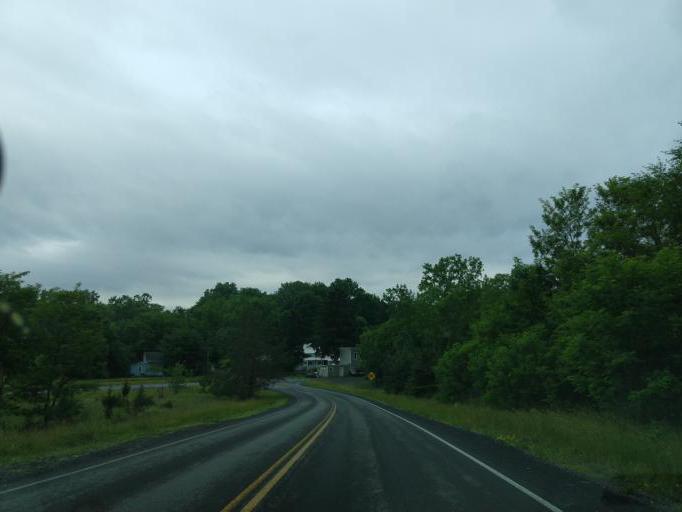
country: US
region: New York
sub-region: Tompkins County
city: Northwest Ithaca
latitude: 42.5377
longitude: -76.5413
